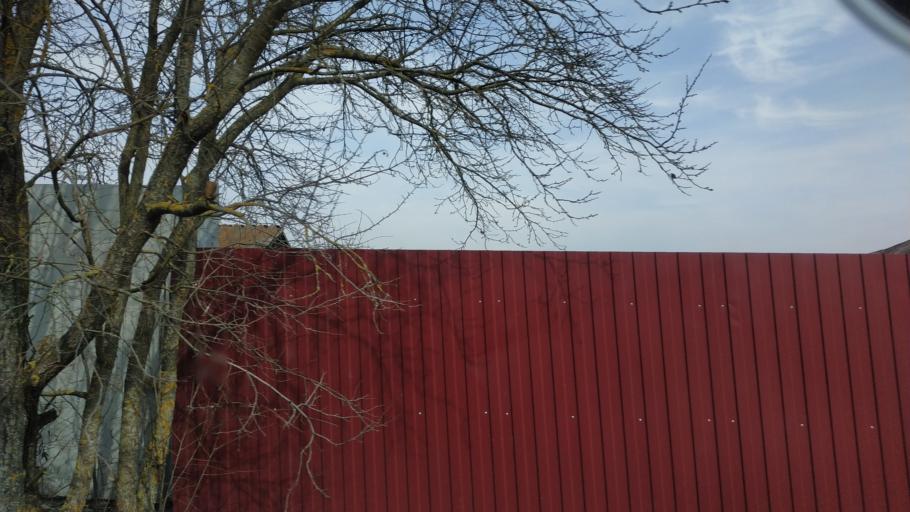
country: RU
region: Moskovskaya
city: Voskresensk
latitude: 55.3449
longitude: 38.6101
